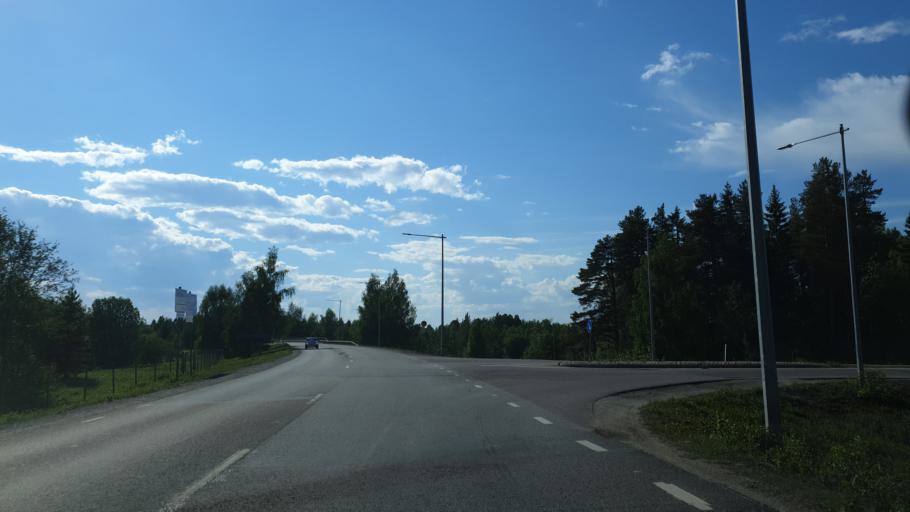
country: SE
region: Norrbotten
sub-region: Pitea Kommun
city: Pitea
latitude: 65.3320
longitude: 21.4454
